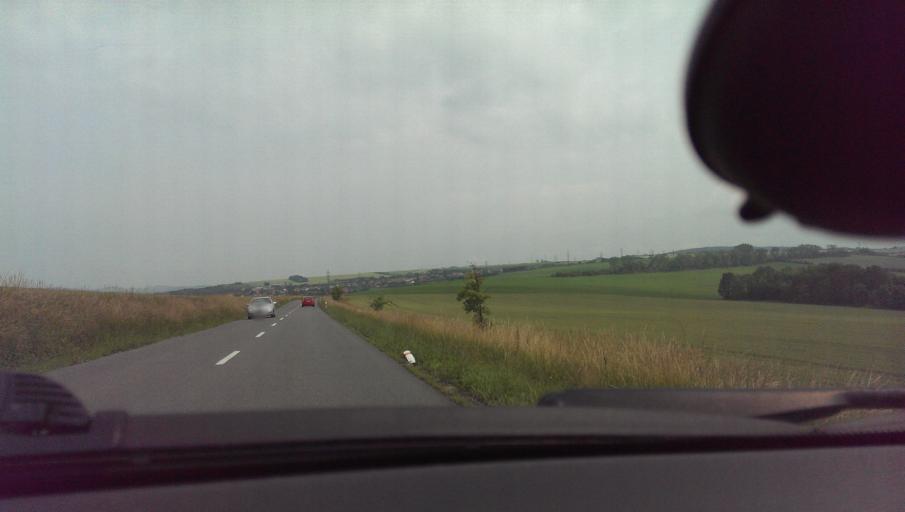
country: CZ
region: Zlin
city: Bilovice
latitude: 49.1067
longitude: 17.5472
